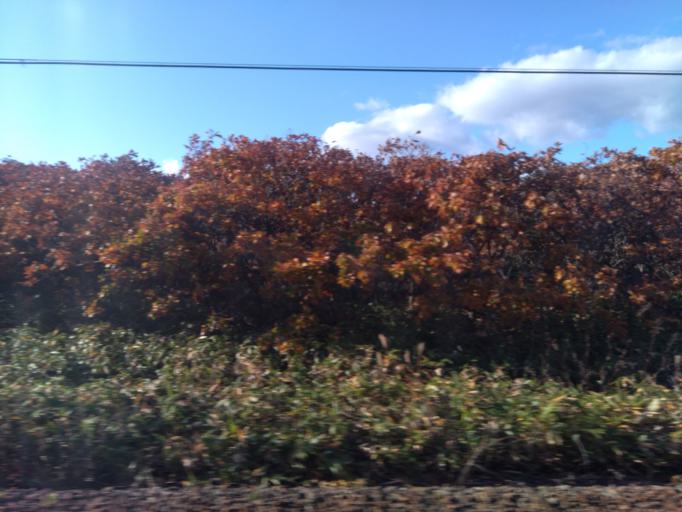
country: JP
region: Hokkaido
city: Niseko Town
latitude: 42.5691
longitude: 140.4400
